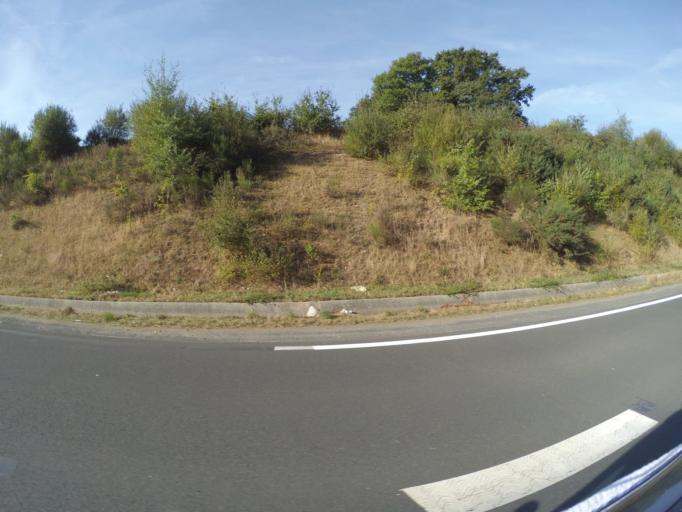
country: FR
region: Pays de la Loire
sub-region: Departement de la Vendee
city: Bouffere
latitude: 46.9622
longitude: -1.3238
